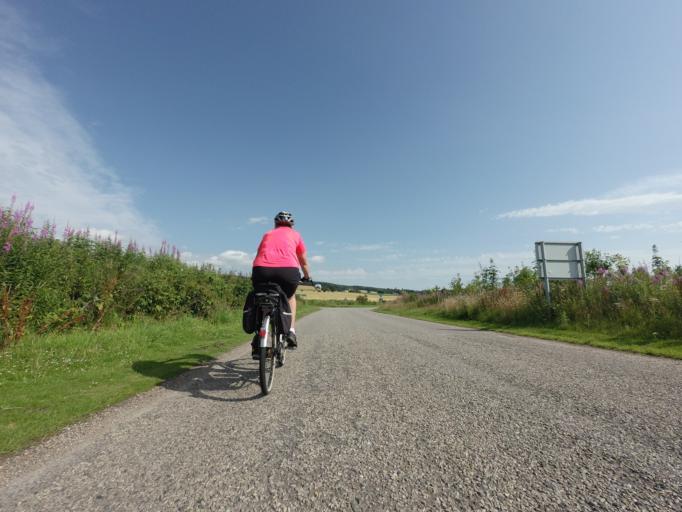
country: GB
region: Scotland
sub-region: Highland
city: Alness
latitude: 57.7097
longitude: -4.2270
